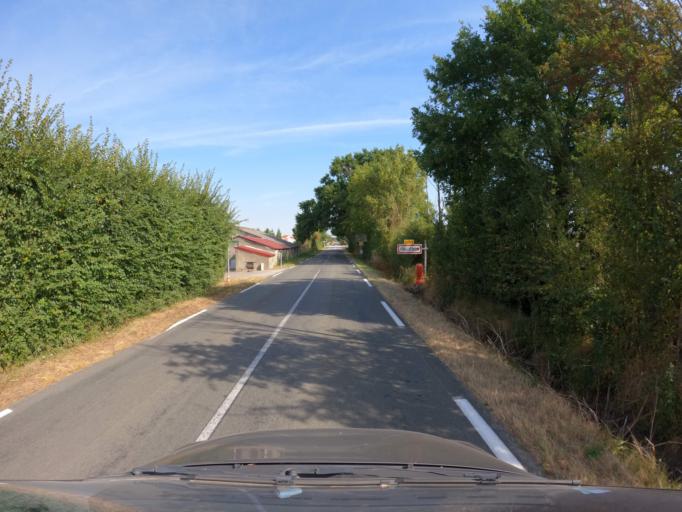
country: FR
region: Pays de la Loire
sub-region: Departement de la Vendee
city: Falleron
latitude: 46.8757
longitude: -1.7035
